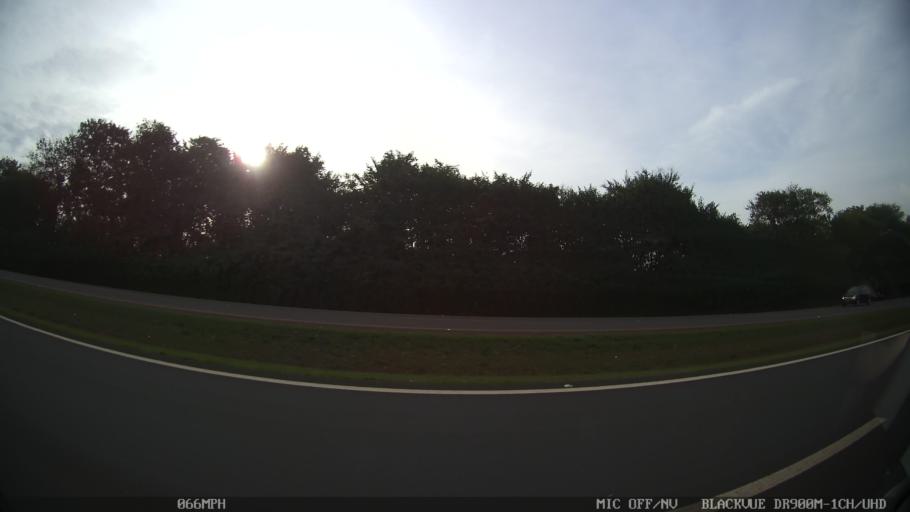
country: BR
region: Sao Paulo
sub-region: Iracemapolis
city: Iracemapolis
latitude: -22.6630
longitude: -47.5312
